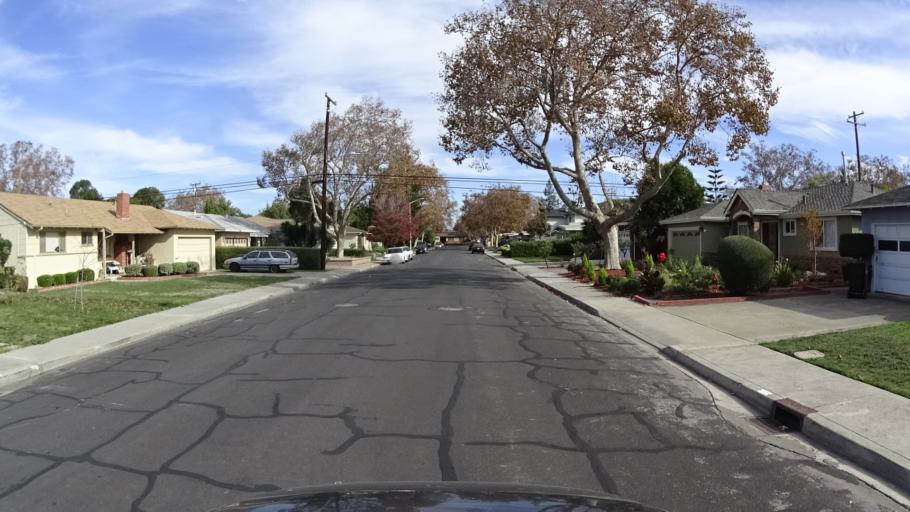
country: US
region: California
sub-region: Santa Clara County
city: Santa Clara
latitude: 37.3583
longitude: -121.9671
